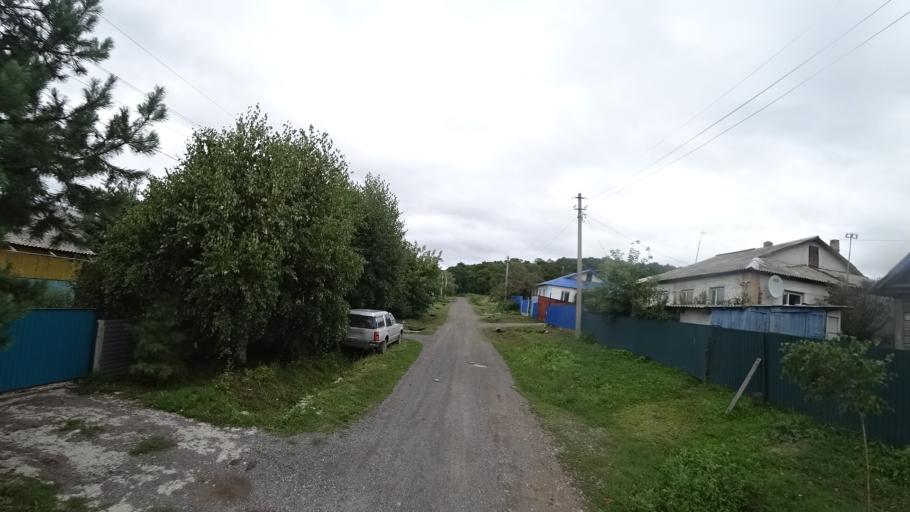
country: RU
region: Primorskiy
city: Chernigovka
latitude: 44.4577
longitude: 132.5962
